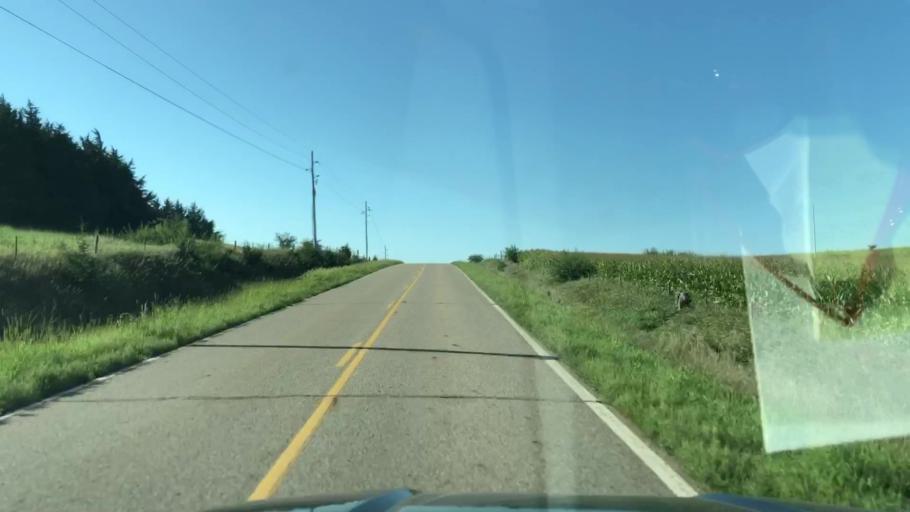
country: US
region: Iowa
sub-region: Woodbury County
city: Sergeant Bluff
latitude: 42.4322
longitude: -96.2136
